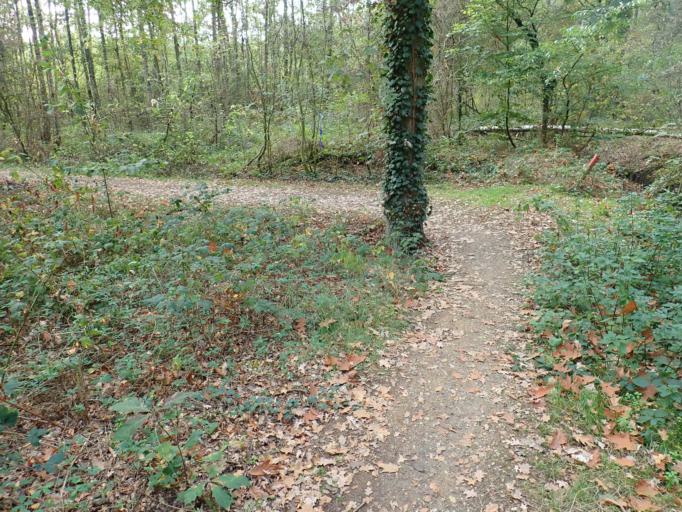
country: BE
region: Flanders
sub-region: Provincie Antwerpen
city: Herenthout
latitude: 51.1393
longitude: 4.7404
